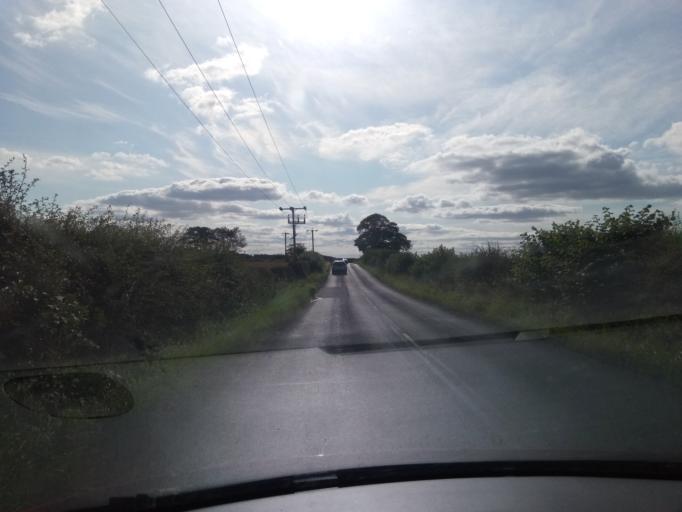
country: GB
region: Scotland
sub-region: The Scottish Borders
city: Chirnside
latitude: 55.7611
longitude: -2.1203
